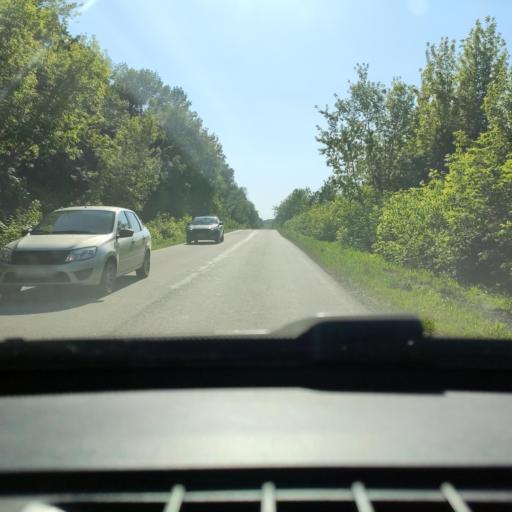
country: RU
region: Voronezj
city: Pereleshinskiy
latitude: 51.6189
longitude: 40.2507
